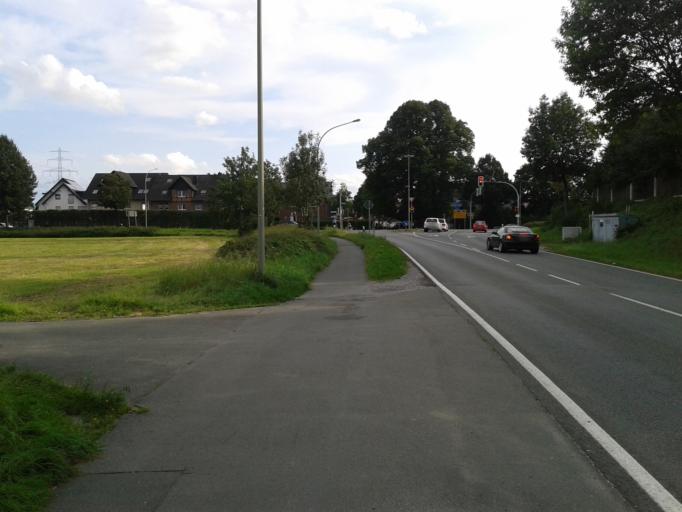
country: DE
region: North Rhine-Westphalia
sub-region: Regierungsbezirk Detmold
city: Paderborn
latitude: 51.7338
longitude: 8.6994
